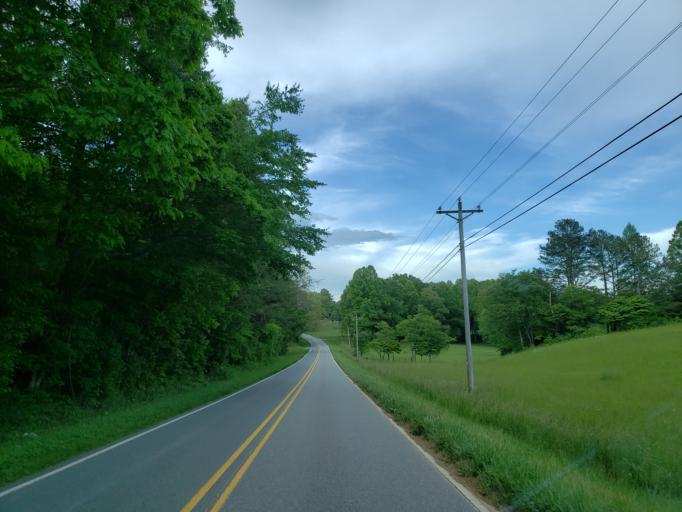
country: US
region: Georgia
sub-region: Fannin County
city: Blue Ridge
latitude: 34.8542
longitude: -84.3785
